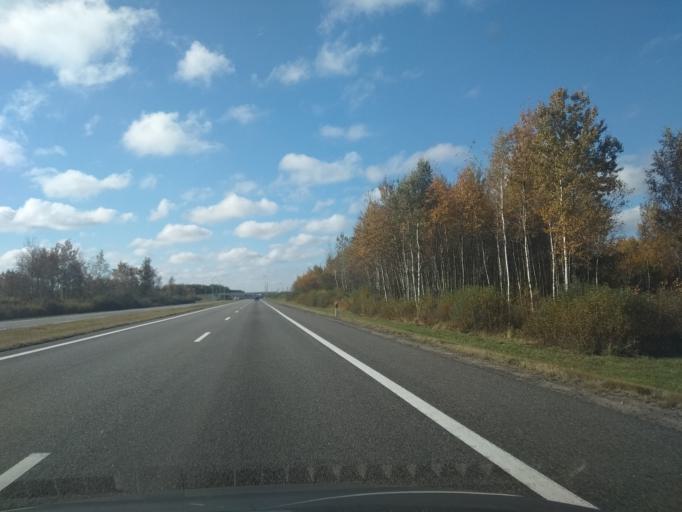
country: BY
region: Minsk
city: Dzyarzhynsk
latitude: 53.6775
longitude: 27.1857
